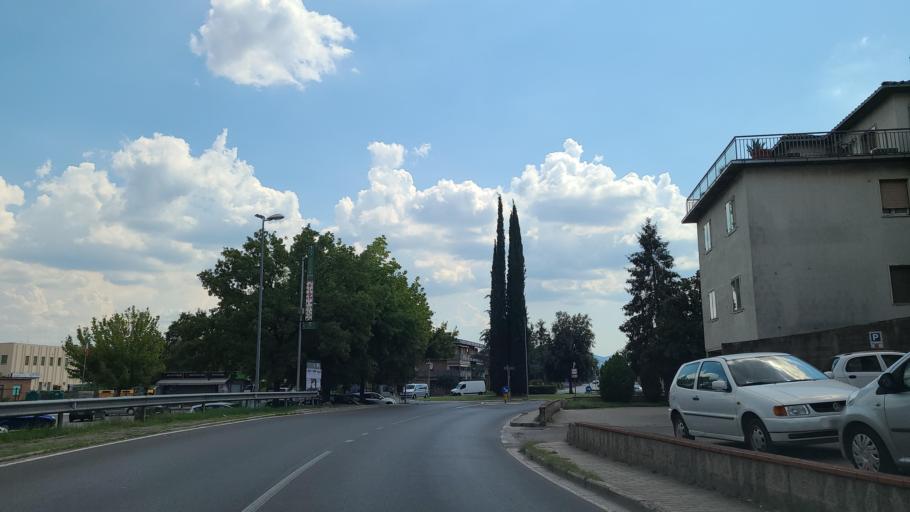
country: IT
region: Tuscany
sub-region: Provincia di Siena
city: Colle di Val d'Elsa
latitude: 43.4165
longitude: 11.1315
